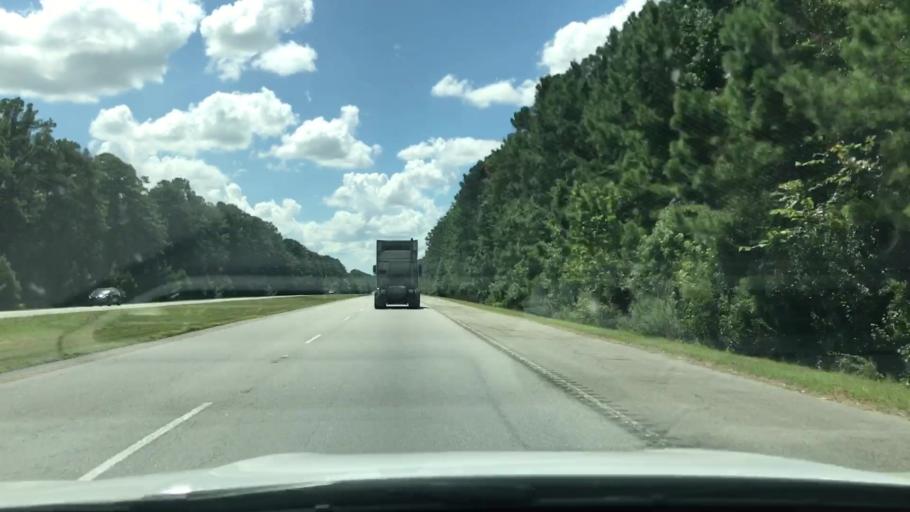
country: US
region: South Carolina
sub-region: Berkeley County
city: Hanahan
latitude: 32.9455
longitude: -79.9991
